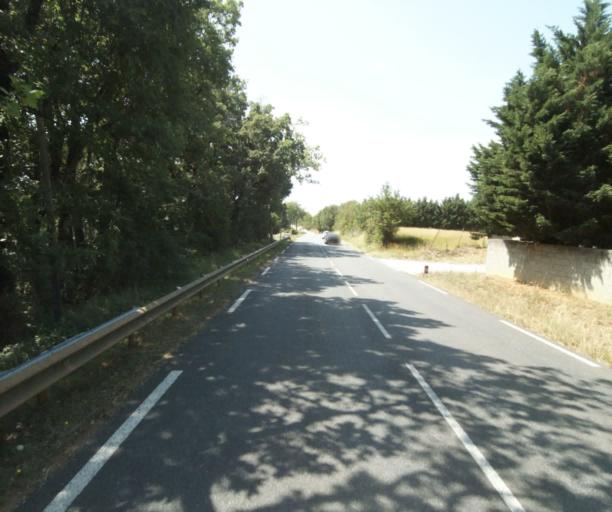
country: FR
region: Midi-Pyrenees
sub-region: Departement de la Haute-Garonne
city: Saint-Felix-Lauragais
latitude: 43.4543
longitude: 1.8722
